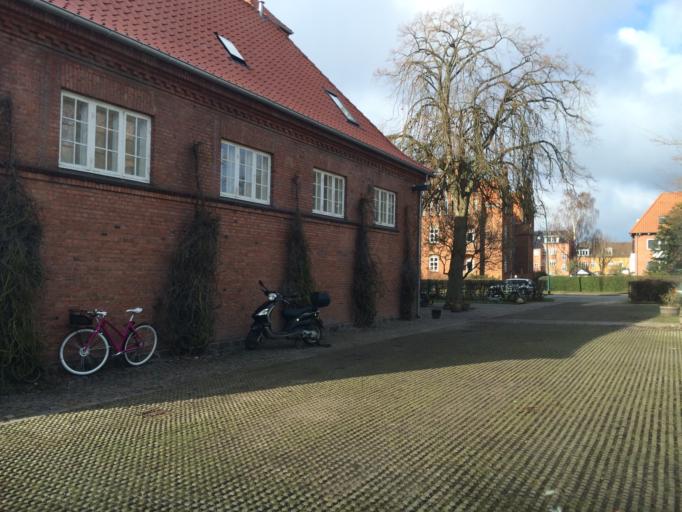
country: DK
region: South Denmark
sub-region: Fredericia Kommune
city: Fredericia
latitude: 55.5695
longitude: 9.7687
